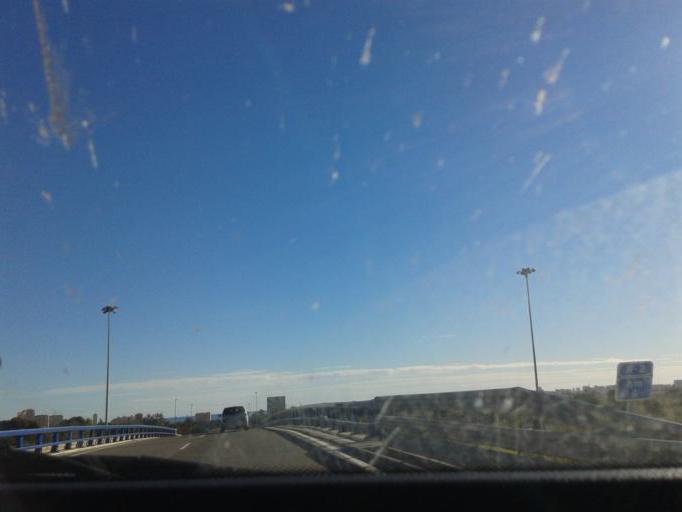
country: ES
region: Valencia
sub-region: Provincia de Alicante
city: Muchamiel
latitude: 38.4198
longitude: -0.4260
